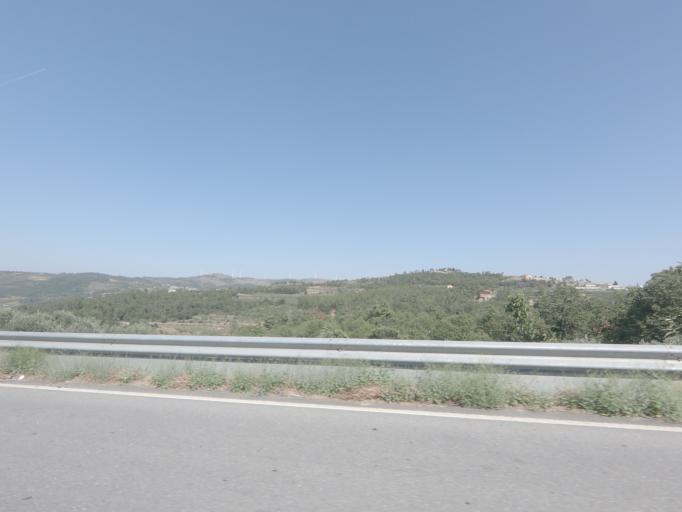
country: PT
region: Viseu
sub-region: Tarouca
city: Tarouca
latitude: 41.0375
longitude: -7.7327
